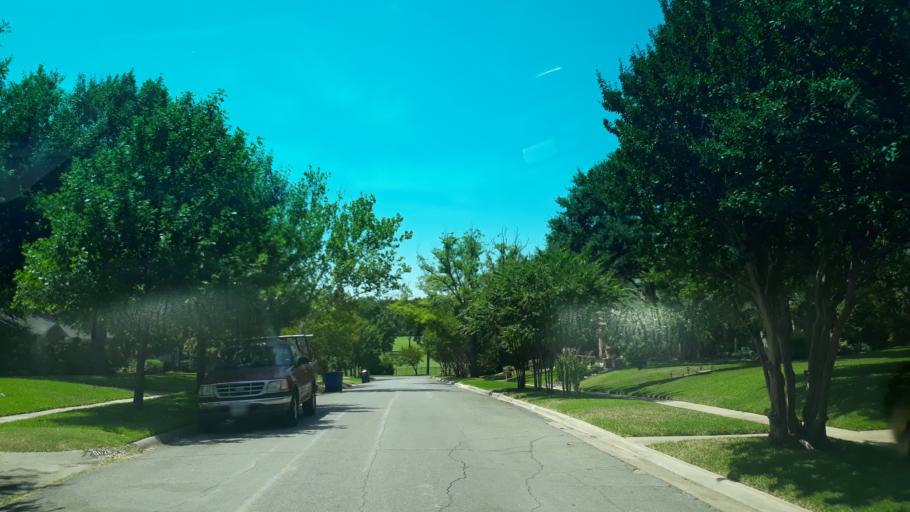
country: US
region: Texas
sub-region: Dallas County
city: Highland Park
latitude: 32.8126
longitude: -96.7426
